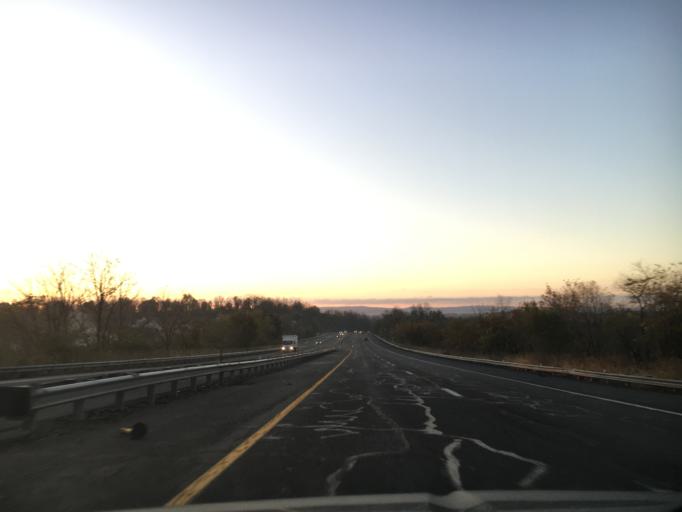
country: US
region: Pennsylvania
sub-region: Lehigh County
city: Egypt
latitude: 40.6826
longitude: -75.5203
